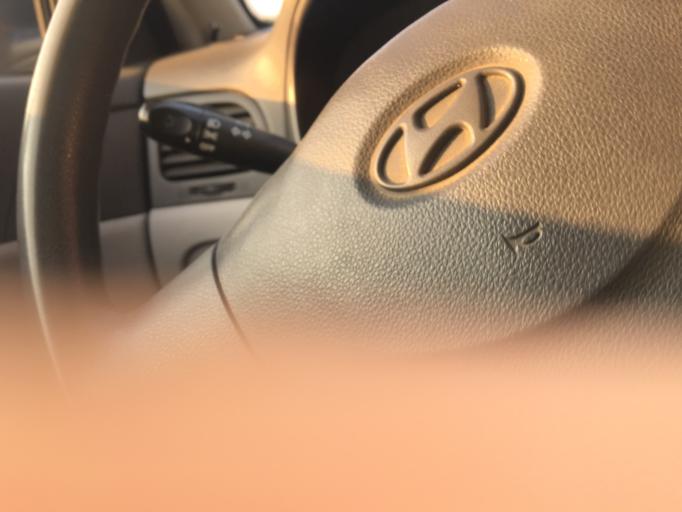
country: EG
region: Muhafazat al Qahirah
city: Cairo
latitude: 30.0464
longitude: 31.2317
